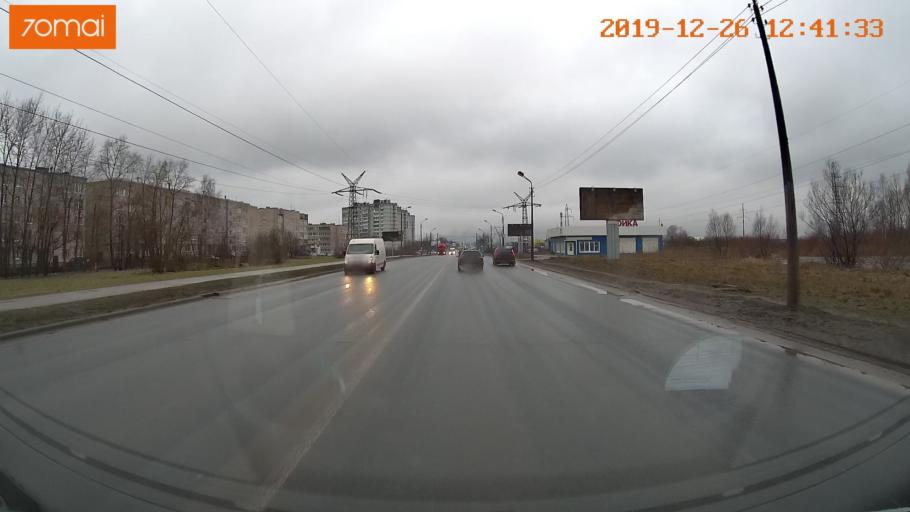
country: RU
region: Vologda
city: Tonshalovo
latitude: 59.1494
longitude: 37.9591
